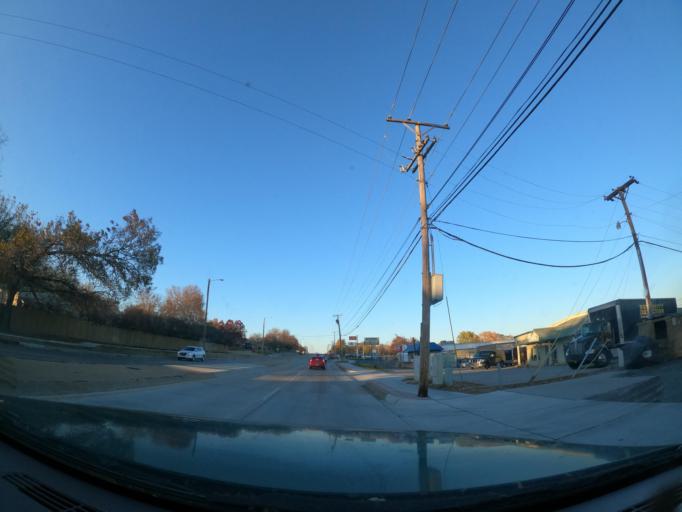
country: US
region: Oklahoma
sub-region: Tulsa County
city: Tulsa
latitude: 36.1262
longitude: -95.8866
